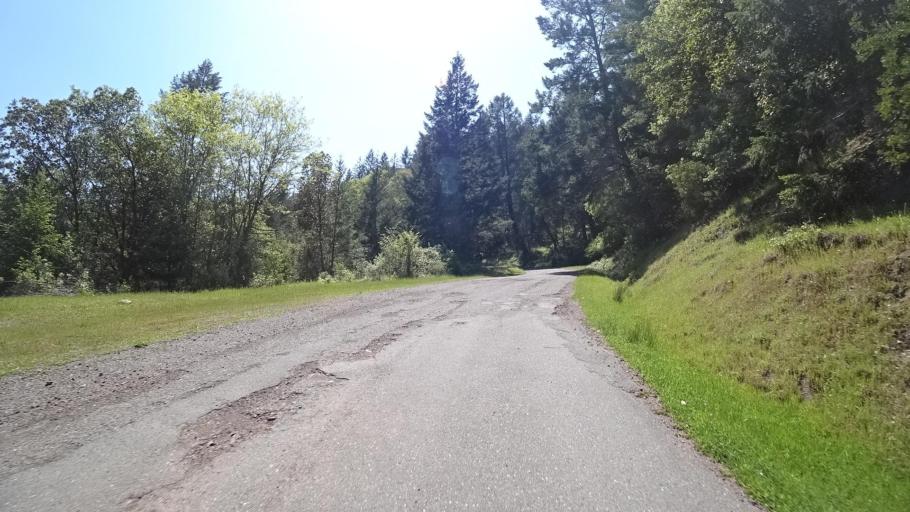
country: US
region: California
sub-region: Humboldt County
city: Redway
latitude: 40.2170
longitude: -123.6575
